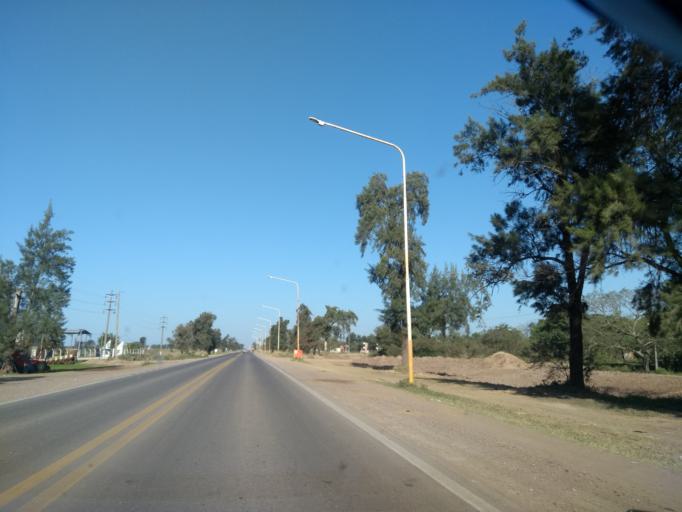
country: AR
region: Chaco
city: Presidencia Roque Saenz Pena
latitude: -26.7943
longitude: -60.4104
